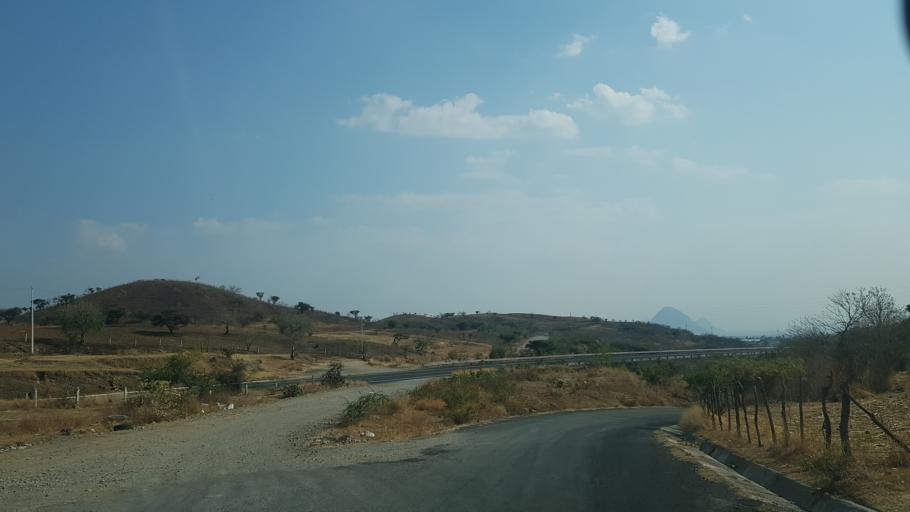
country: MX
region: Morelos
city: Tlacotepec
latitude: 18.8000
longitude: -98.7105
